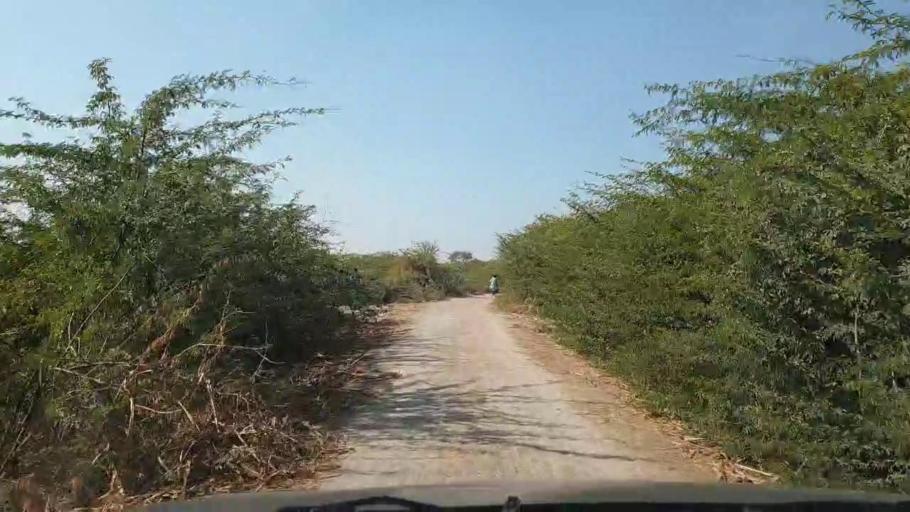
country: PK
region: Sindh
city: Jhol
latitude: 25.9106
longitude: 68.8248
